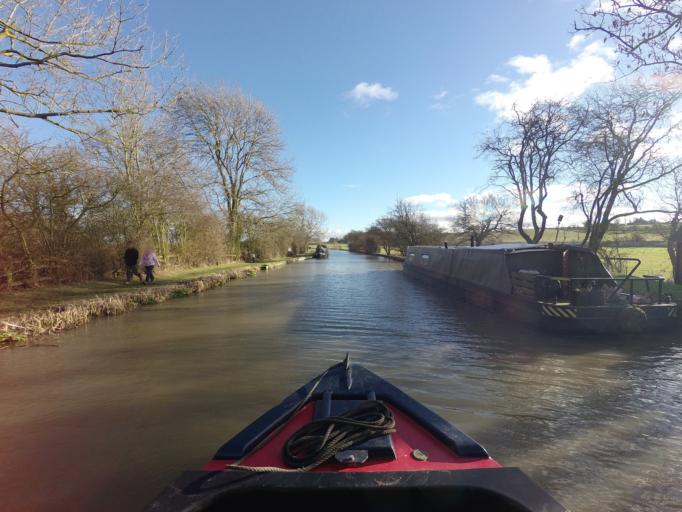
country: GB
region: England
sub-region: Northamptonshire
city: Blisworth
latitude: 52.1938
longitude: -0.9657
